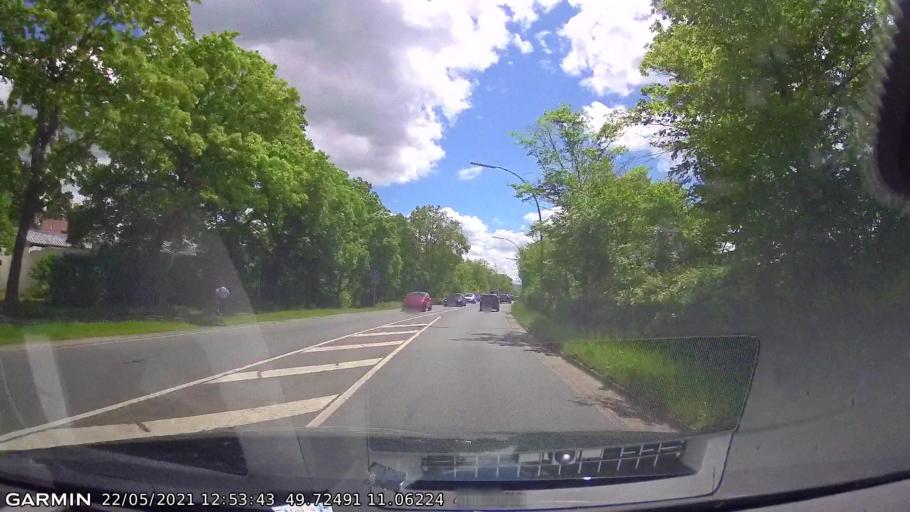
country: DE
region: Bavaria
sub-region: Upper Franconia
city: Forchheim
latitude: 49.7248
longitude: 11.0624
